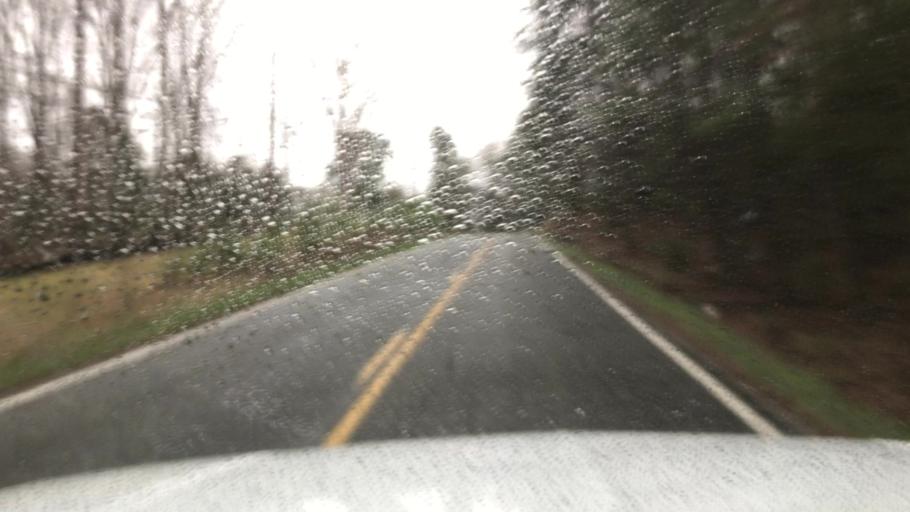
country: US
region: Virginia
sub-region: Henrico County
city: Short Pump
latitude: 37.6448
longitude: -77.6793
